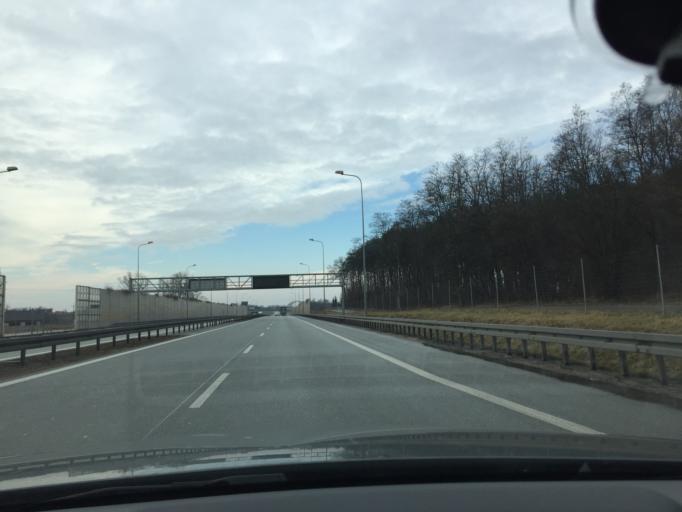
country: PL
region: Lodz Voivodeship
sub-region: Powiat skierniewicki
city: Kowiesy
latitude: 51.9243
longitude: 20.4612
